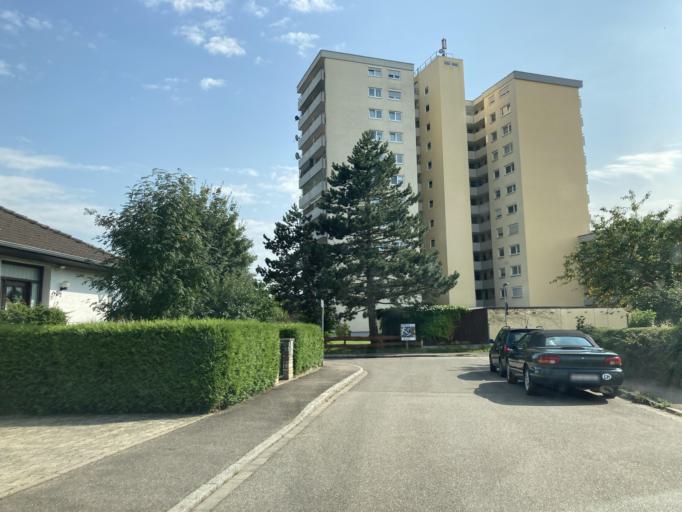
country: DE
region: Baden-Wuerttemberg
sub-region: Freiburg Region
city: Neuenburg am Rhein
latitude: 47.8161
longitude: 7.5704
